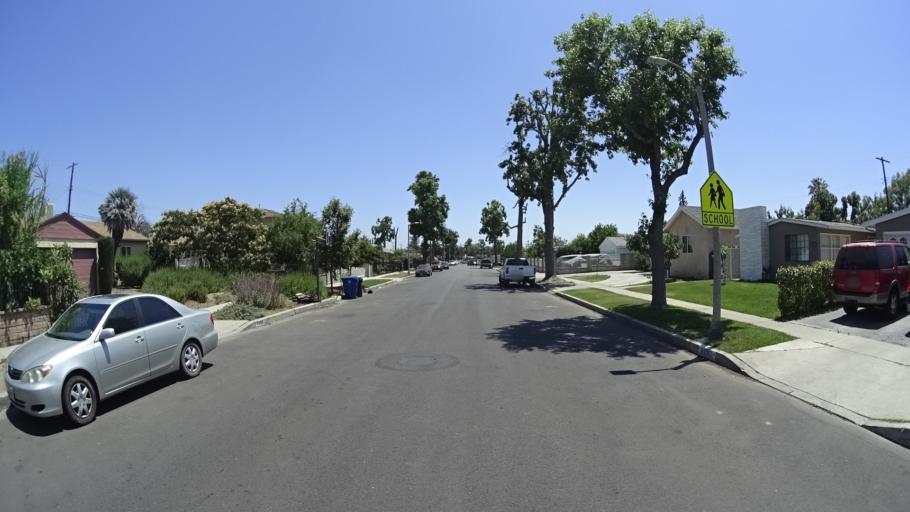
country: US
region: California
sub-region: Los Angeles County
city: Van Nuys
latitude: 34.2167
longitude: -118.4329
